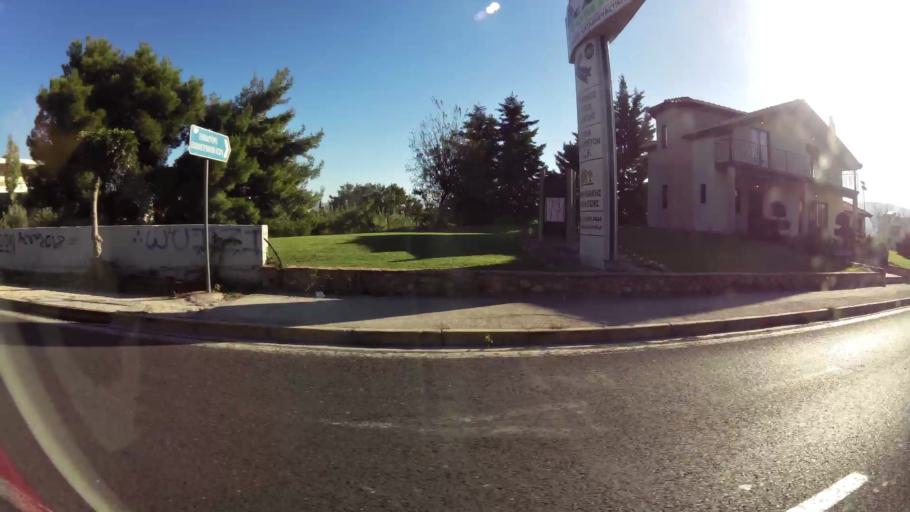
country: GR
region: Attica
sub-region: Nomarchia Anatolikis Attikis
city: Pallini
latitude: 38.0044
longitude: 23.8906
